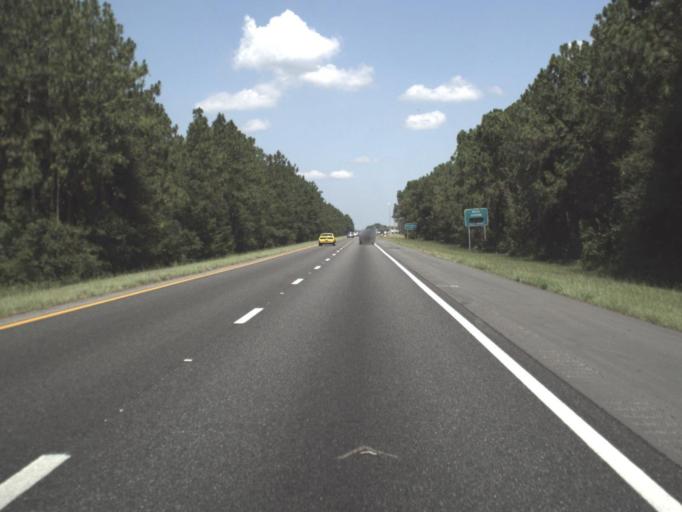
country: US
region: Florida
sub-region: Madison County
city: Madison
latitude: 30.3708
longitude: -83.2567
